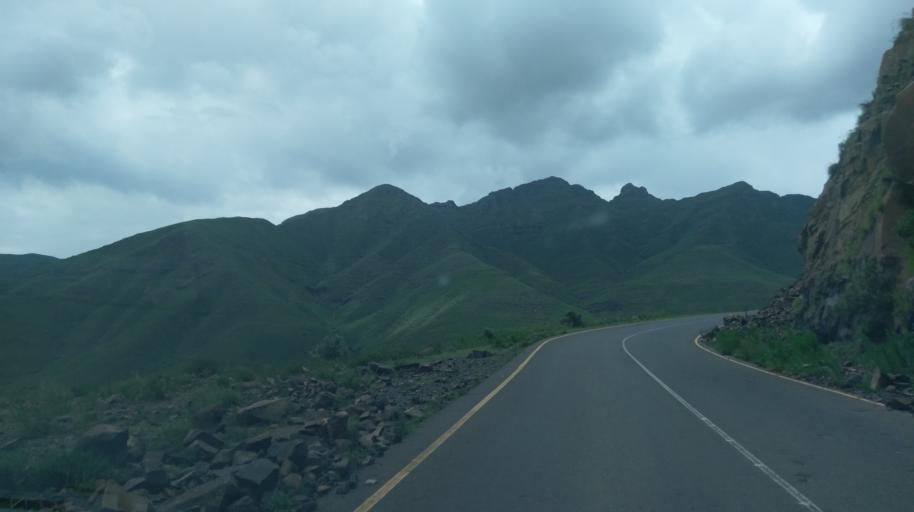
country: LS
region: Butha-Buthe
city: Butha-Buthe
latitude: -29.0548
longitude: 28.3459
